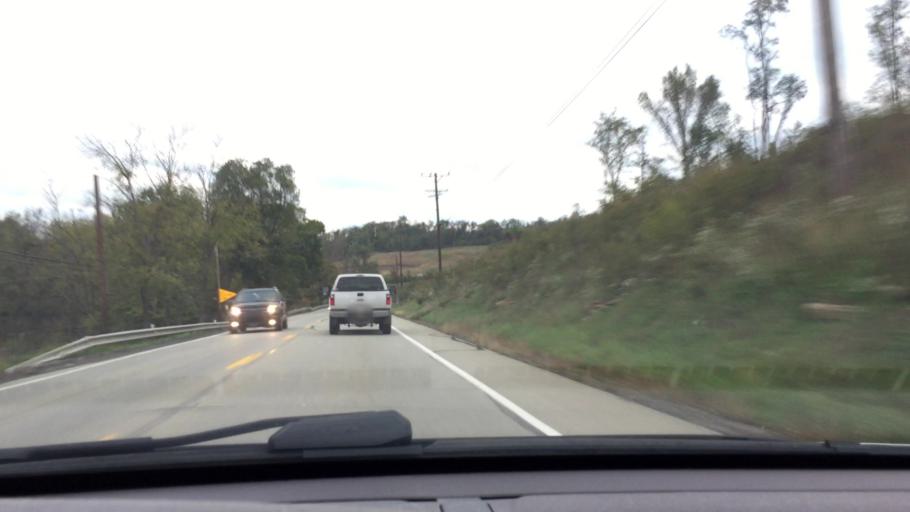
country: US
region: Pennsylvania
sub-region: Washington County
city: Canonsburg
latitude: 40.2329
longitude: -80.1677
